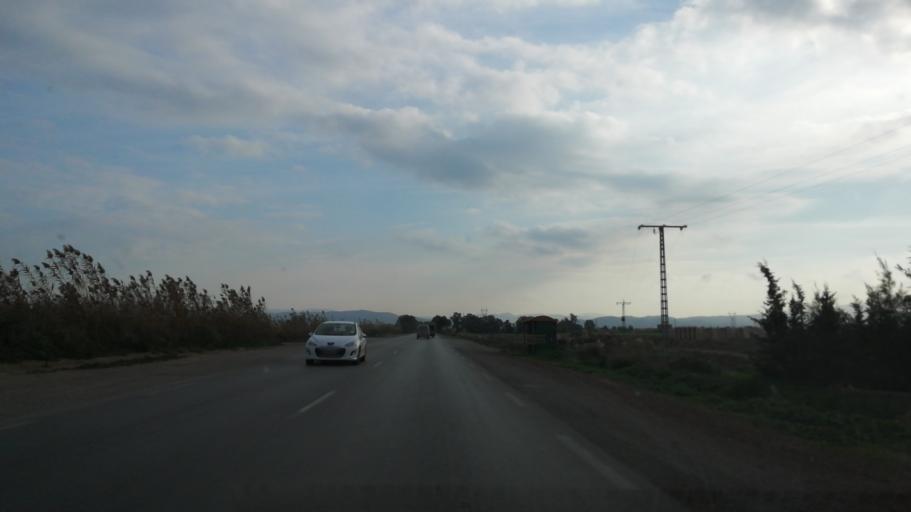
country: DZ
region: Mascara
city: Mascara
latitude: 35.6430
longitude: 0.0602
